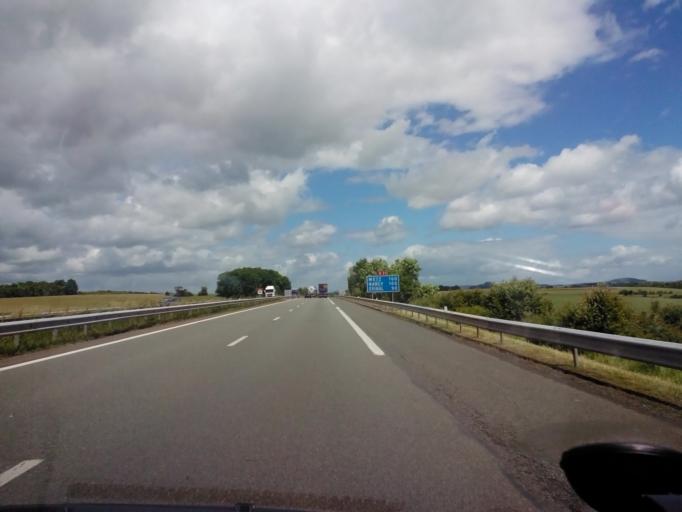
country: FR
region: Champagne-Ardenne
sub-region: Departement de la Haute-Marne
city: Avrecourt
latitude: 48.0022
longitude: 5.5160
